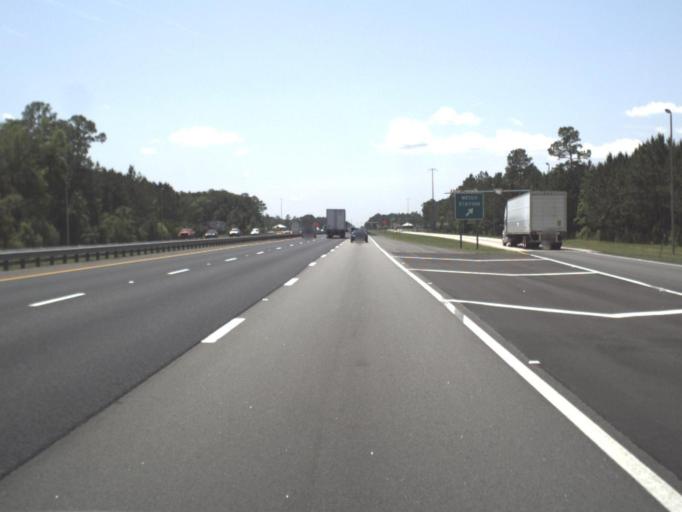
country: US
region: Florida
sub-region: Nassau County
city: Yulee
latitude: 30.6775
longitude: -81.6706
